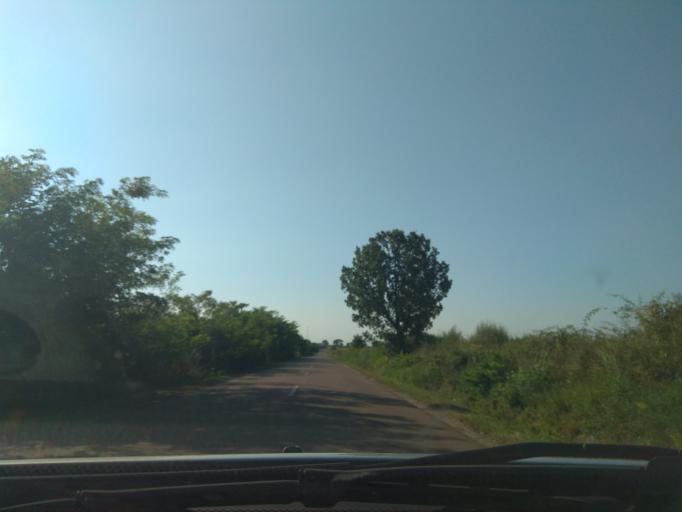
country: HU
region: Borsod-Abauj-Zemplen
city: Emod
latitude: 47.9598
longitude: 20.8047
